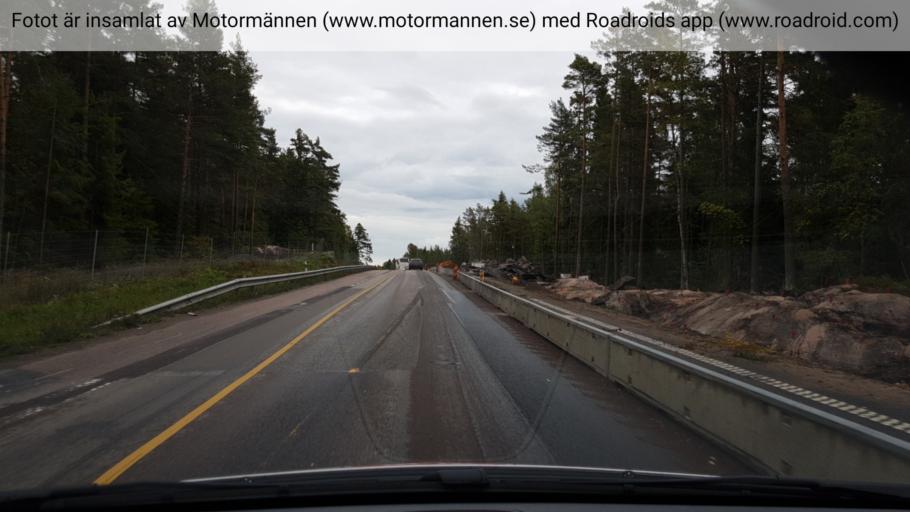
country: SE
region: Vaermland
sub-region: Hammaro Kommun
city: Skoghall
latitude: 59.3807
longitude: 13.3851
